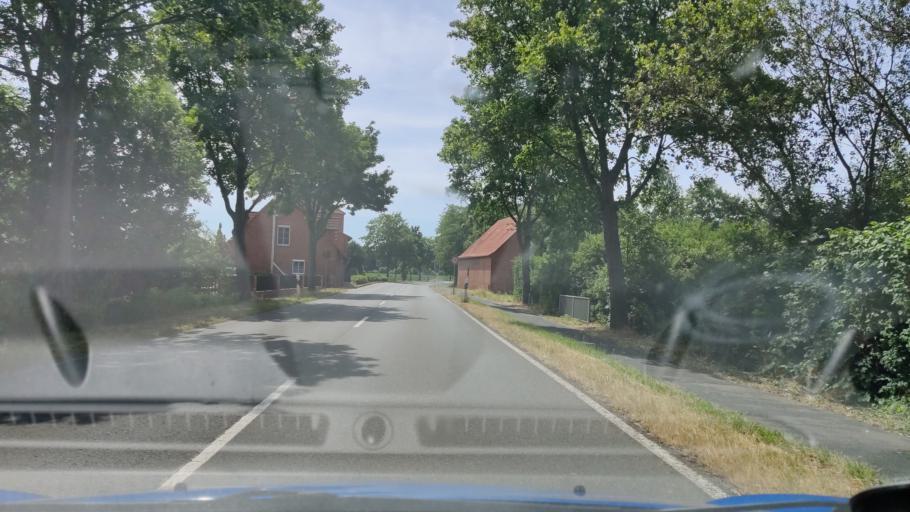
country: DE
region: Lower Saxony
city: Neustadt am Rubenberge
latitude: 52.5321
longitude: 9.4632
